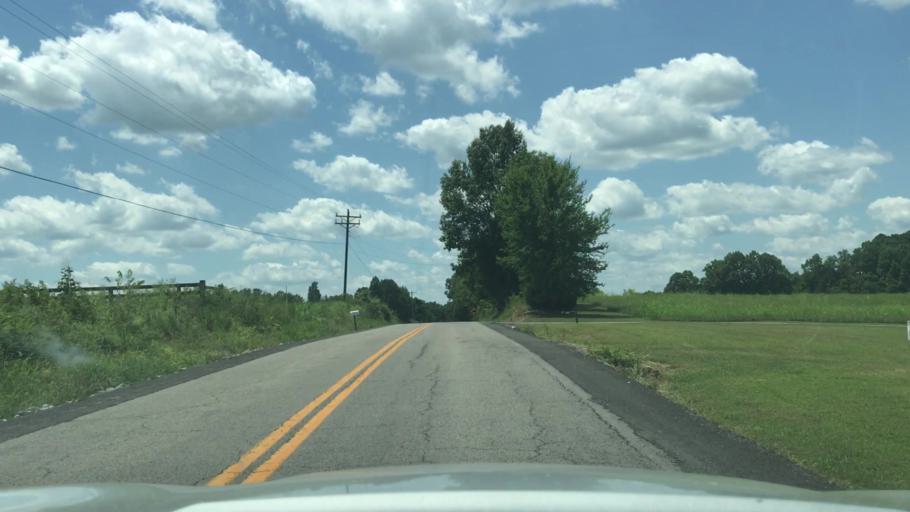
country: US
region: Kentucky
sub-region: Muhlenberg County
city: Greenville
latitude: 37.1274
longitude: -87.3002
